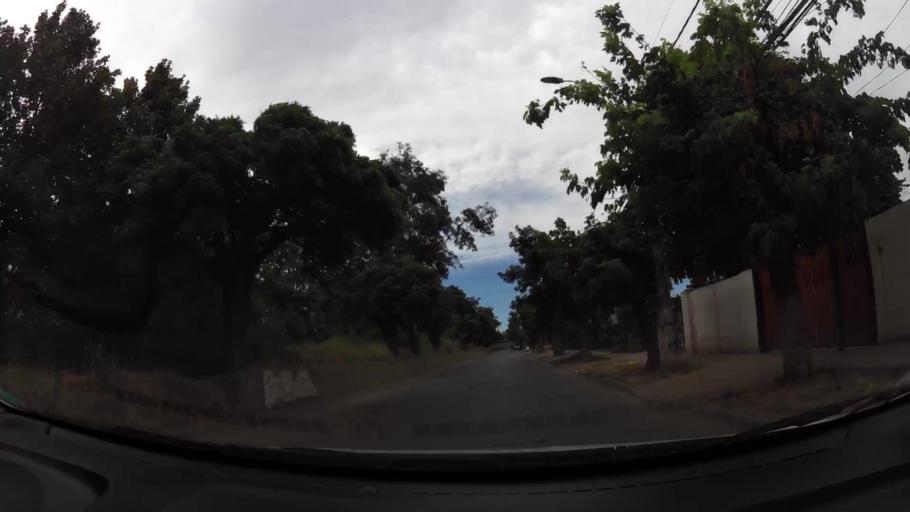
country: CL
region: O'Higgins
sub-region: Provincia de Cachapoal
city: Graneros
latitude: -34.0697
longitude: -70.7260
